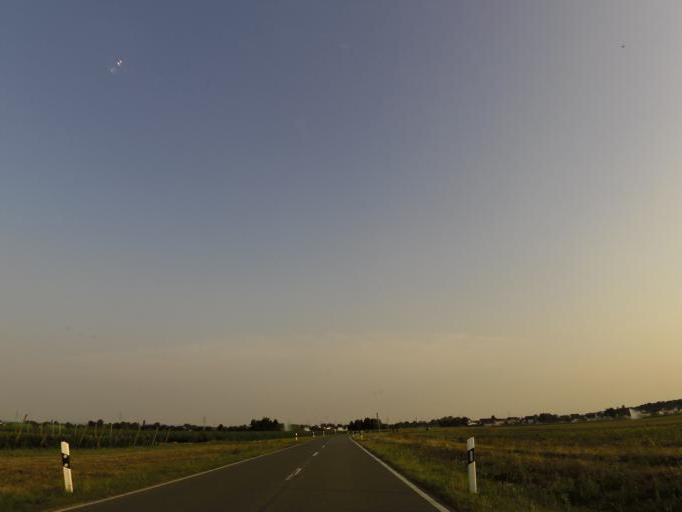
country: DE
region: Hesse
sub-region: Regierungsbezirk Darmstadt
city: Buttelborn
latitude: 49.9402
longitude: 8.5445
